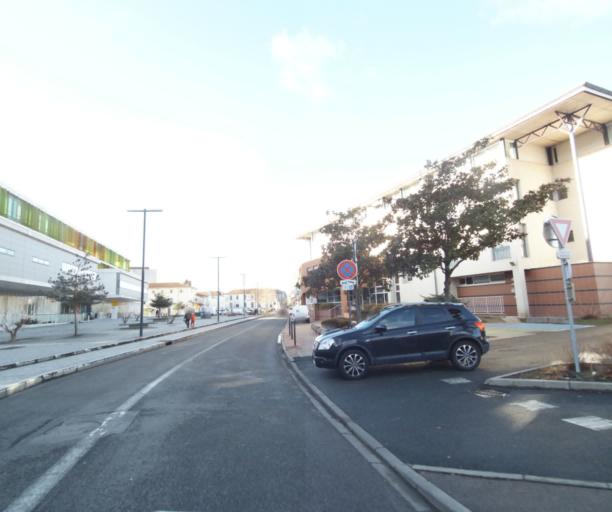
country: FR
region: Rhone-Alpes
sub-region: Departement de la Loire
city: Roanne
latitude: 46.0430
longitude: 4.0779
